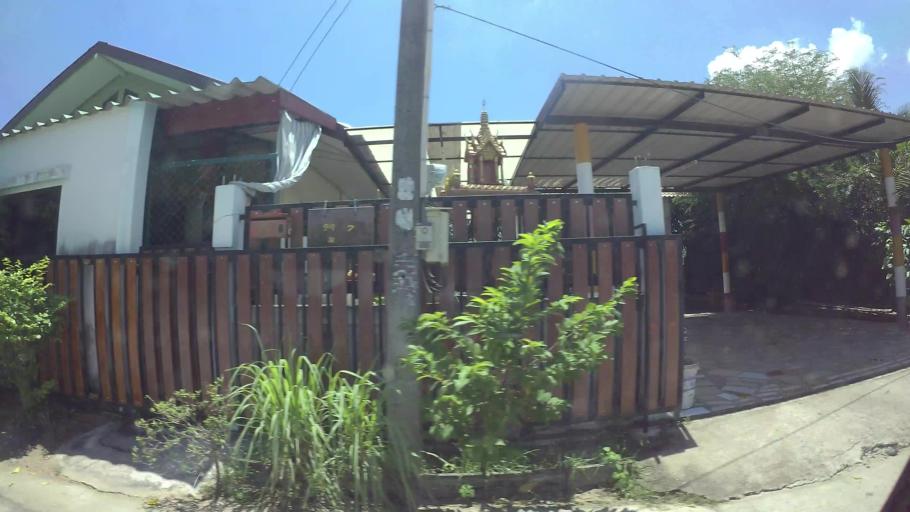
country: TH
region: Chon Buri
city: Si Racha
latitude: 13.1353
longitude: 100.9443
